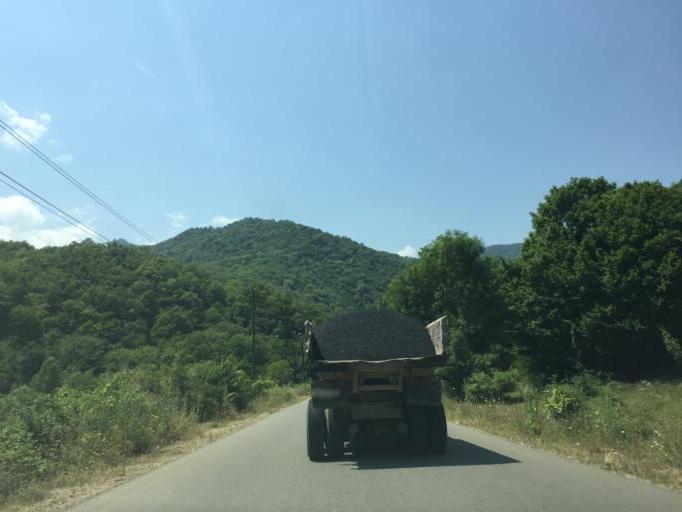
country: AZ
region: Kalbacar Rayonu
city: Kerbakhiar
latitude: 40.1240
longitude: 46.4278
